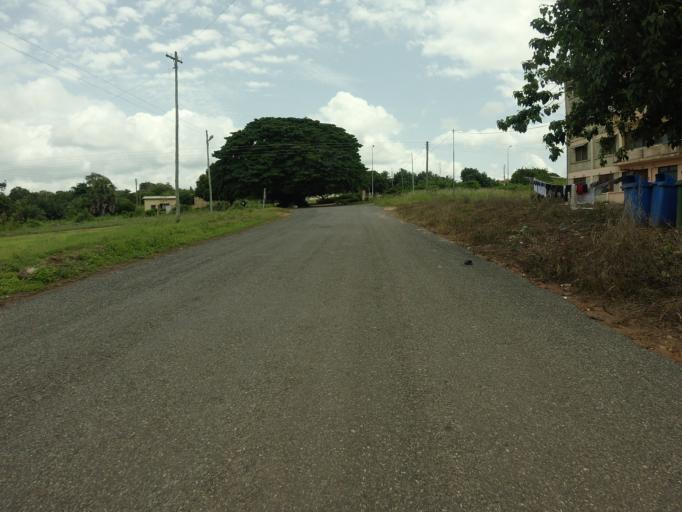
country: GH
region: Volta
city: Ho
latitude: 6.5983
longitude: 0.4801
